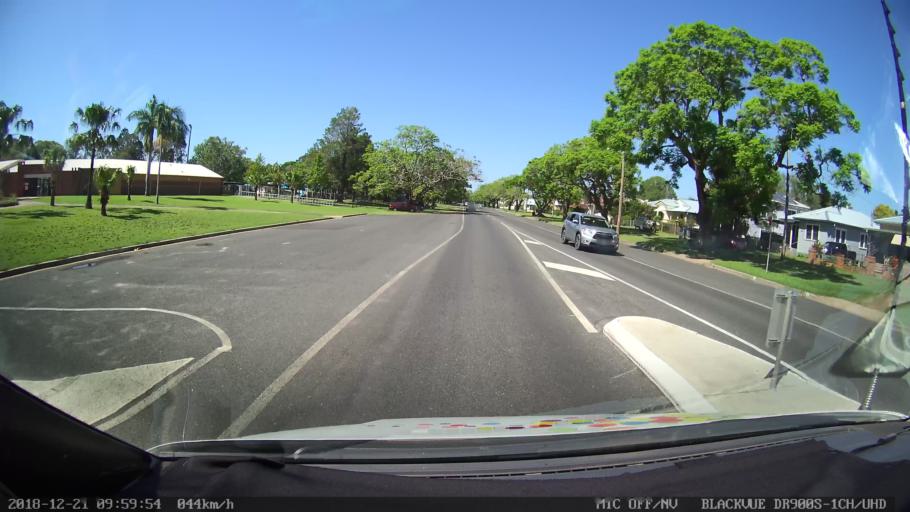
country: AU
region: New South Wales
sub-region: Clarence Valley
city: Grafton
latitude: -29.6810
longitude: 152.9286
